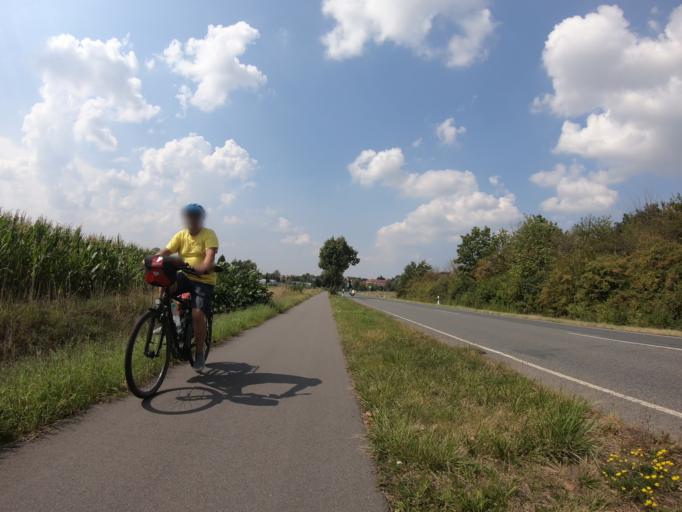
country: DE
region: Lower Saxony
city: Sickte
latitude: 52.2146
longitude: 10.6494
